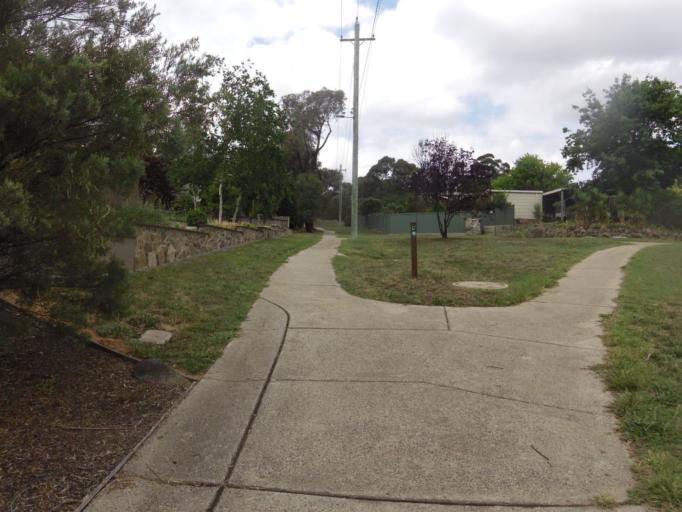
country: AU
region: Australian Capital Territory
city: Macarthur
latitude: -35.4022
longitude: 149.1292
